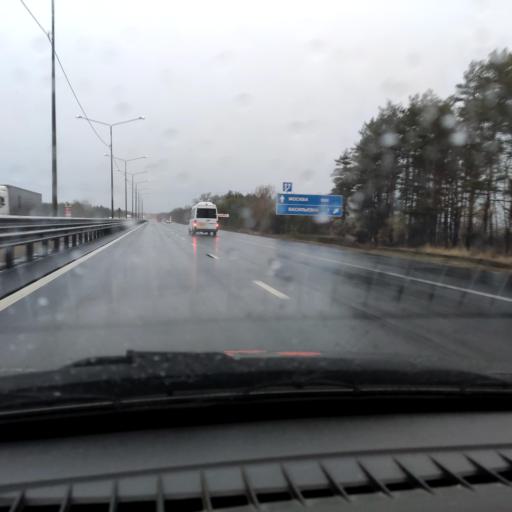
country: RU
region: Samara
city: Zhigulevsk
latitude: 53.5131
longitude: 49.5947
